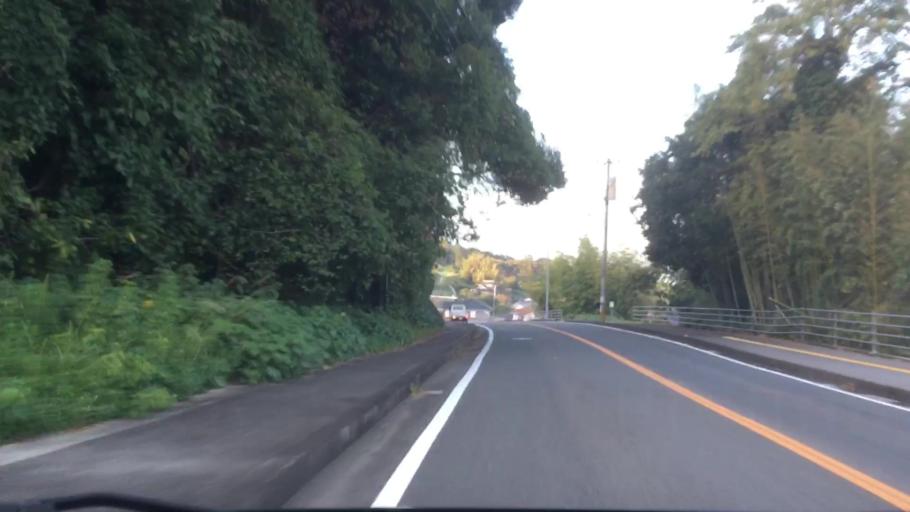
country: JP
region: Nagasaki
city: Sasebo
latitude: 33.0057
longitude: 129.7311
